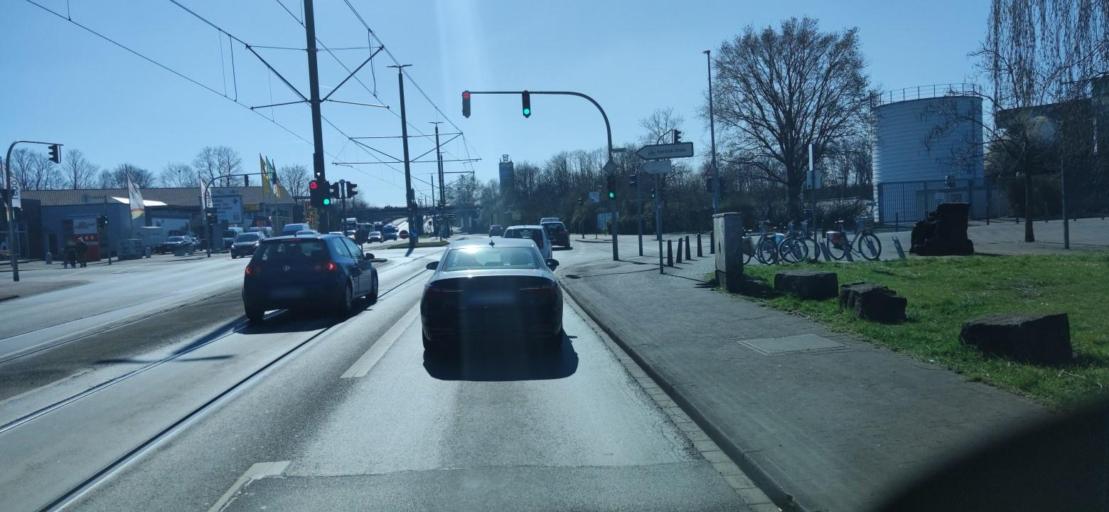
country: DE
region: North Rhine-Westphalia
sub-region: Regierungsbezirk Dusseldorf
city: Hochfeld
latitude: 51.4107
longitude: 6.7523
